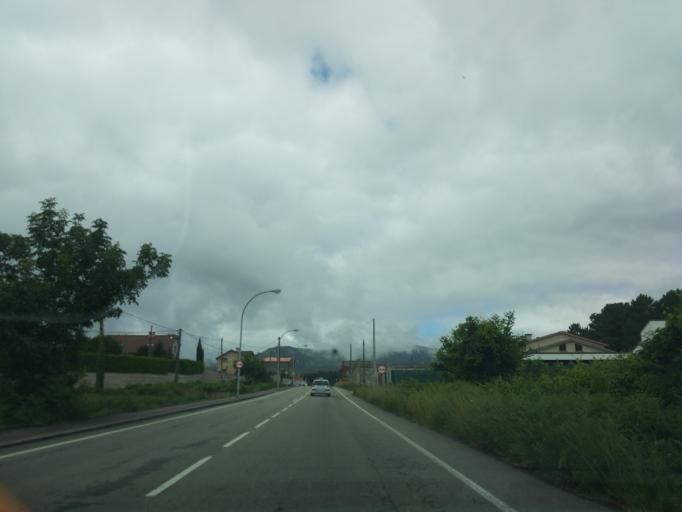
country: ES
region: Galicia
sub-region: Provincia da Coruna
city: Boiro
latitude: 42.6443
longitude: -8.8715
